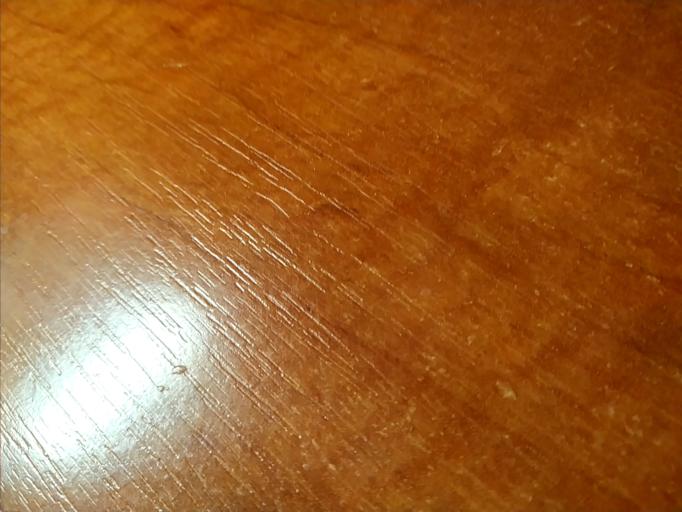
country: RU
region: Vologda
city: Kaduy
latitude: 59.7583
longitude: 37.1818
